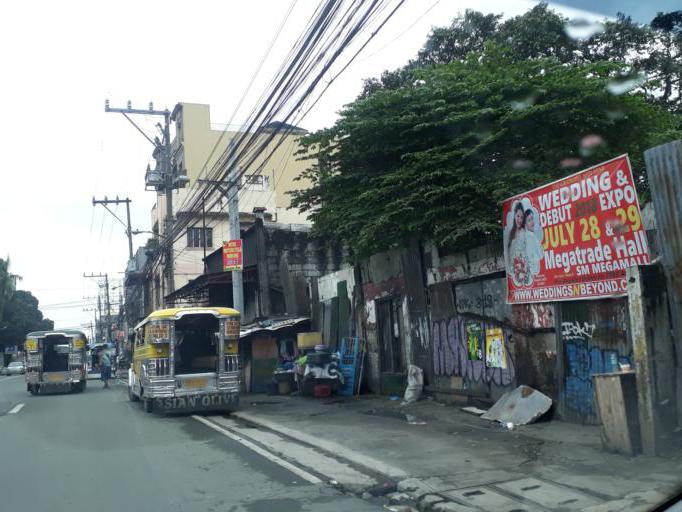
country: PH
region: Calabarzon
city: Del Monte
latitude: 14.6493
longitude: 121.0177
